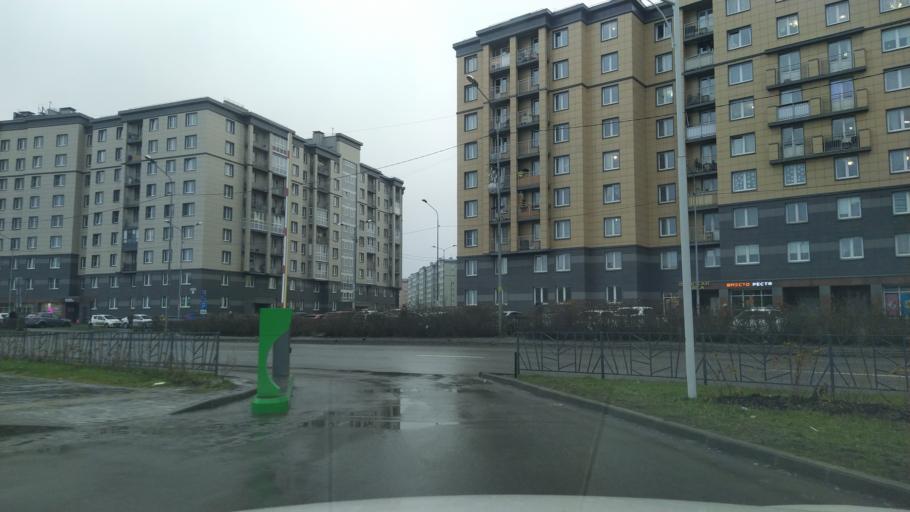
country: RU
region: St.-Petersburg
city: Tyarlevo
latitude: 59.7425
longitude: 30.4708
